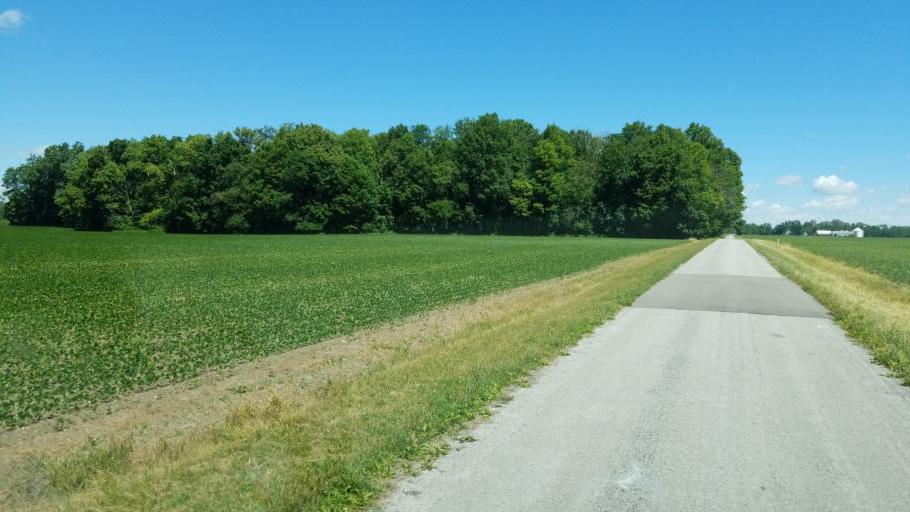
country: US
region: Ohio
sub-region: Morrow County
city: Cardington
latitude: 40.6205
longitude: -82.9427
